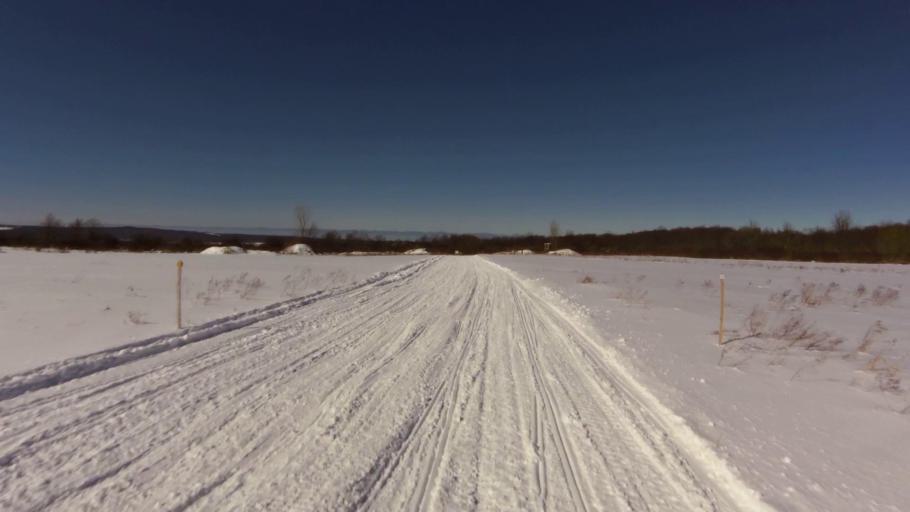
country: US
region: New York
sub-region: Chautauqua County
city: Mayville
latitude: 42.2662
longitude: -79.4516
